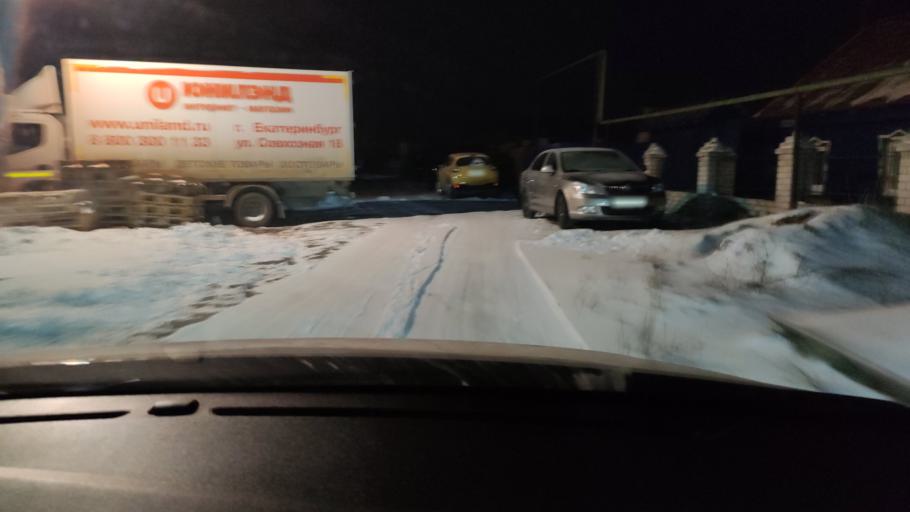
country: RU
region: Tatarstan
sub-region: Gorod Kazan'
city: Kazan
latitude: 55.7505
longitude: 49.1109
